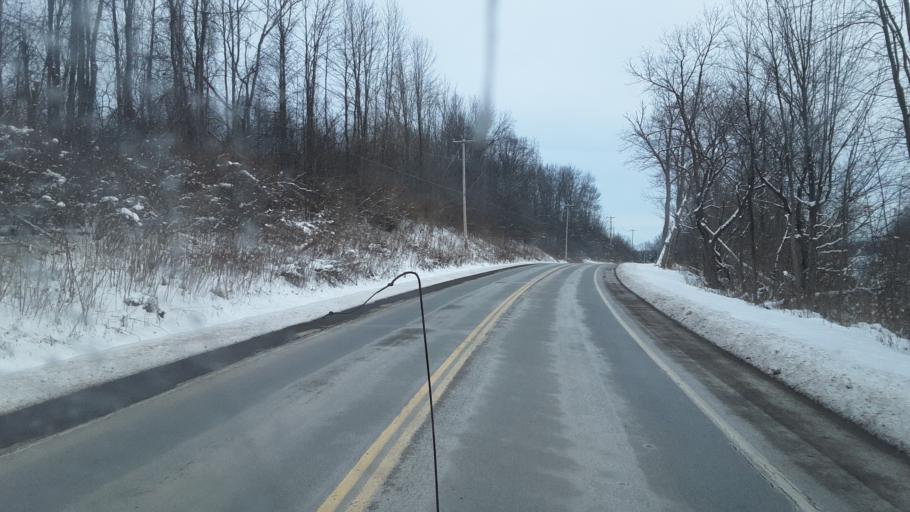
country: US
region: New York
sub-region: Wayne County
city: Newark
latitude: 43.0598
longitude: -77.0582
